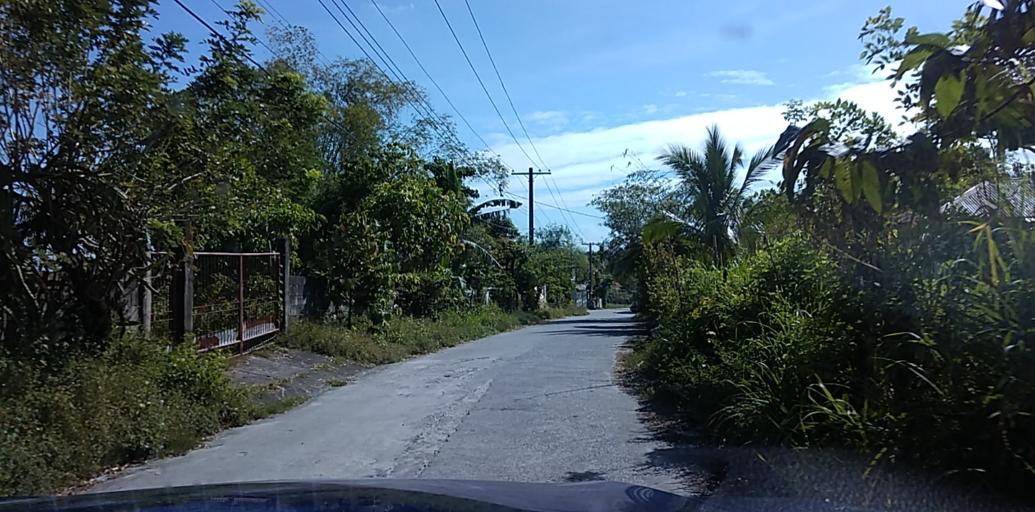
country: PH
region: Central Luzon
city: Santol
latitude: 15.1683
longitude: 120.5028
